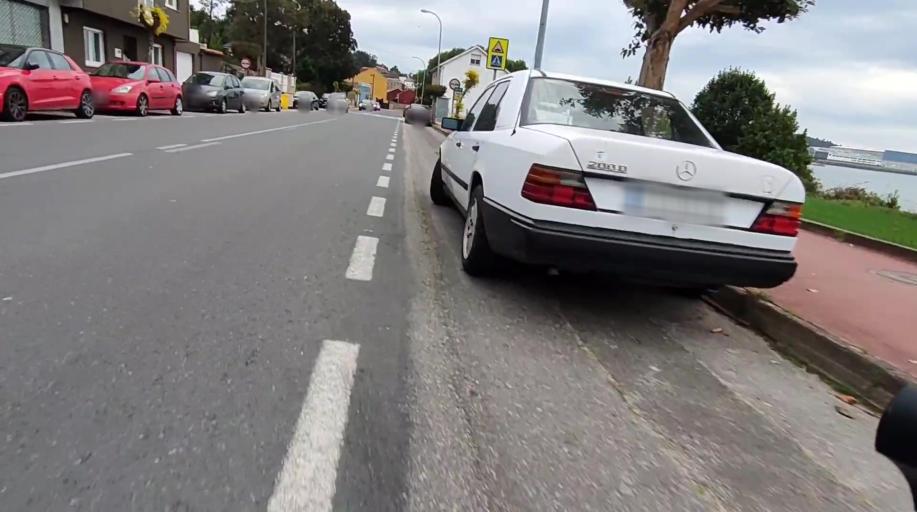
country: ES
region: Galicia
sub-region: Provincia da Coruna
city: Boiro
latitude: 42.6306
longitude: -8.8734
